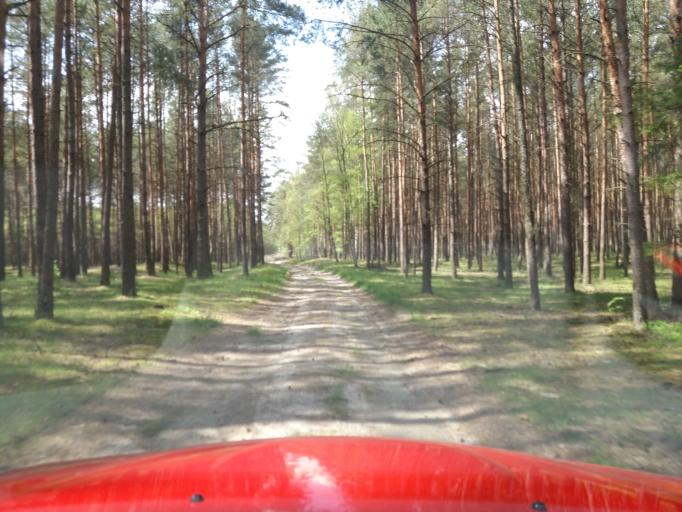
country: PL
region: West Pomeranian Voivodeship
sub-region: Powiat choszczenski
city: Drawno
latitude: 53.1138
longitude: 15.7678
